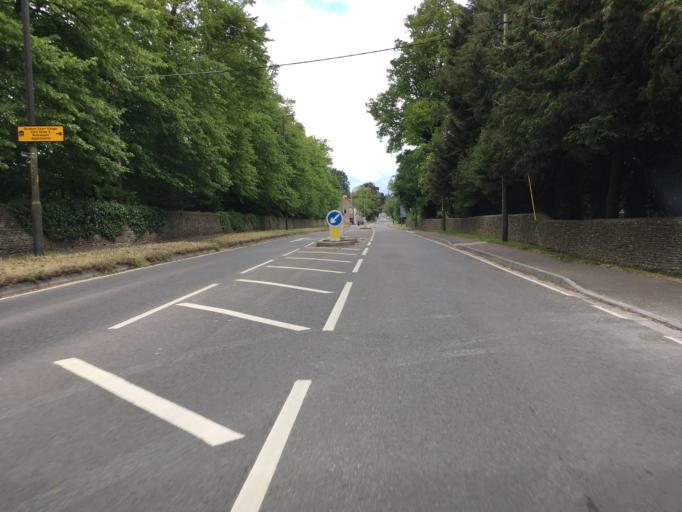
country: GB
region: England
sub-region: Gloucestershire
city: Cirencester
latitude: 51.7281
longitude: -1.9787
